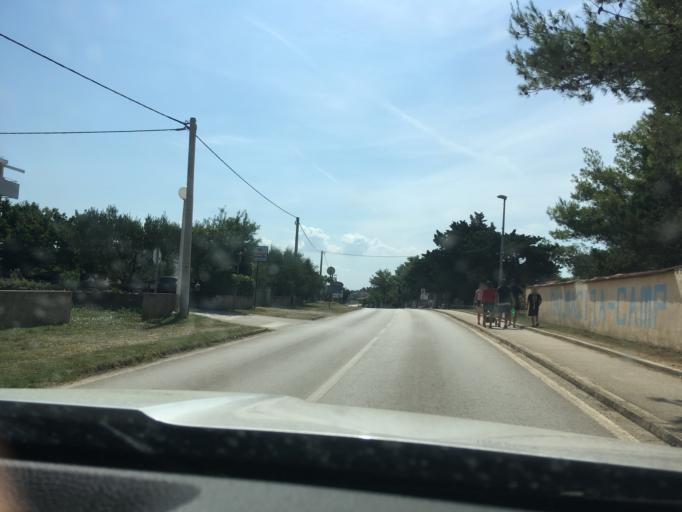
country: HR
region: Zadarska
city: Privlaka
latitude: 44.2574
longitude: 15.1250
